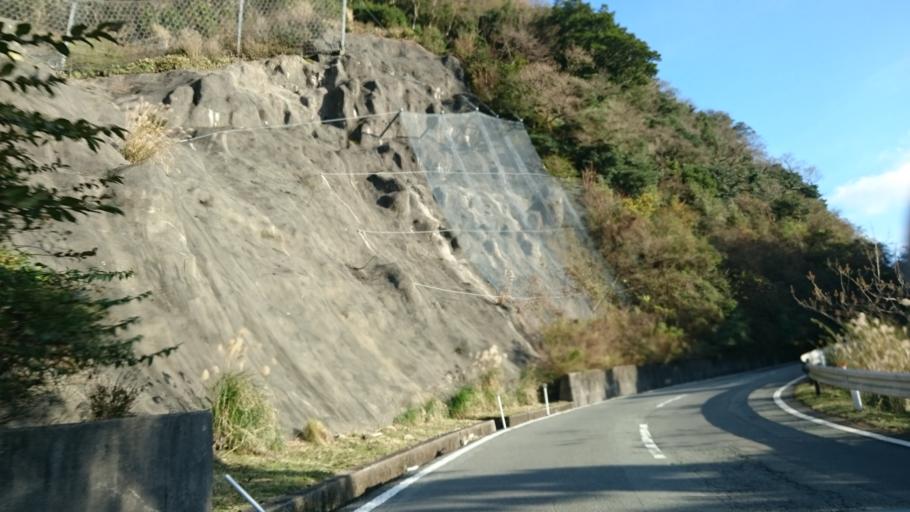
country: JP
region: Shizuoka
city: Heda
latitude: 34.9732
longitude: 138.8317
